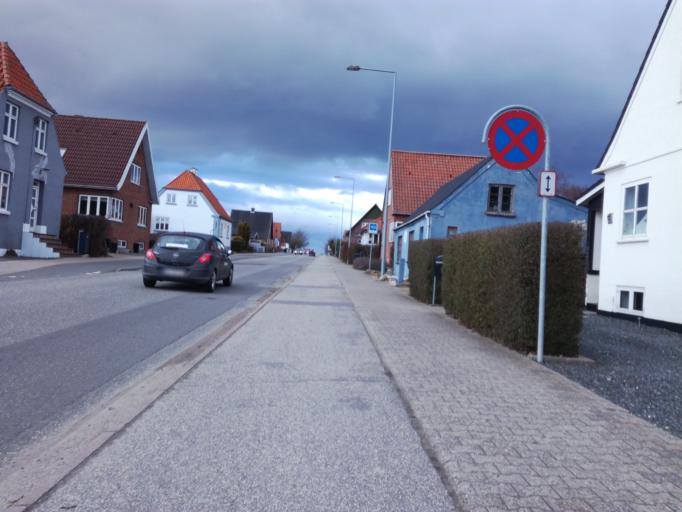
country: DK
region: South Denmark
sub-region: Fredericia Kommune
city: Fredericia
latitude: 55.5786
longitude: 9.7671
